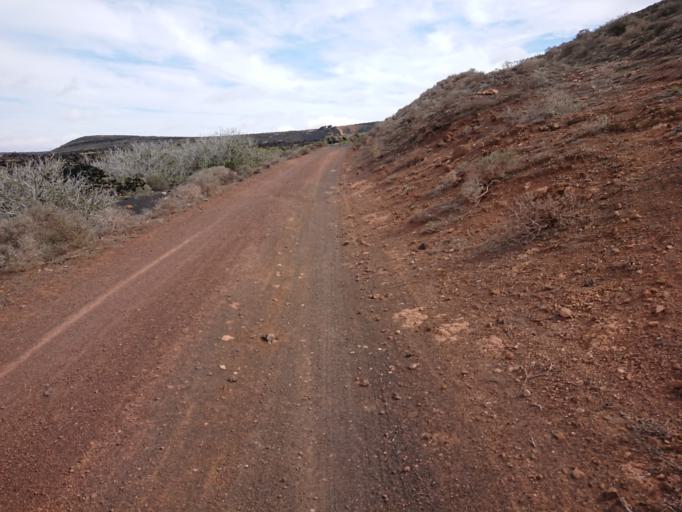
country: ES
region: Canary Islands
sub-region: Provincia de Las Palmas
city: Tinajo
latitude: 29.0205
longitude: -13.6777
